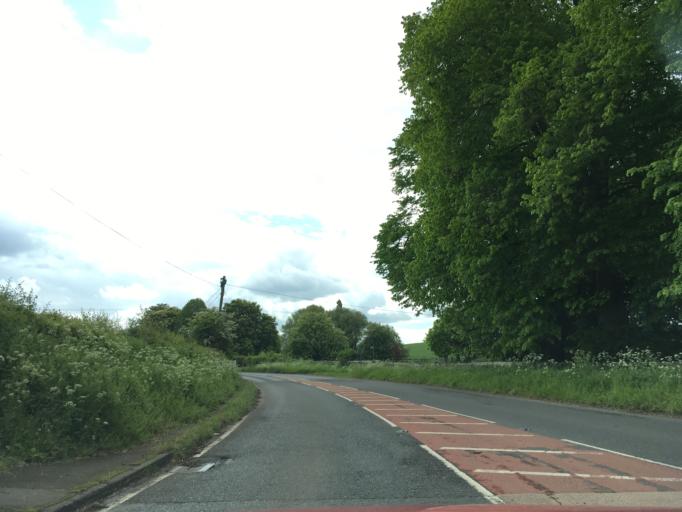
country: GB
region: England
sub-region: Gloucestershire
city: Stonehouse
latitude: 51.7745
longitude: -2.2899
